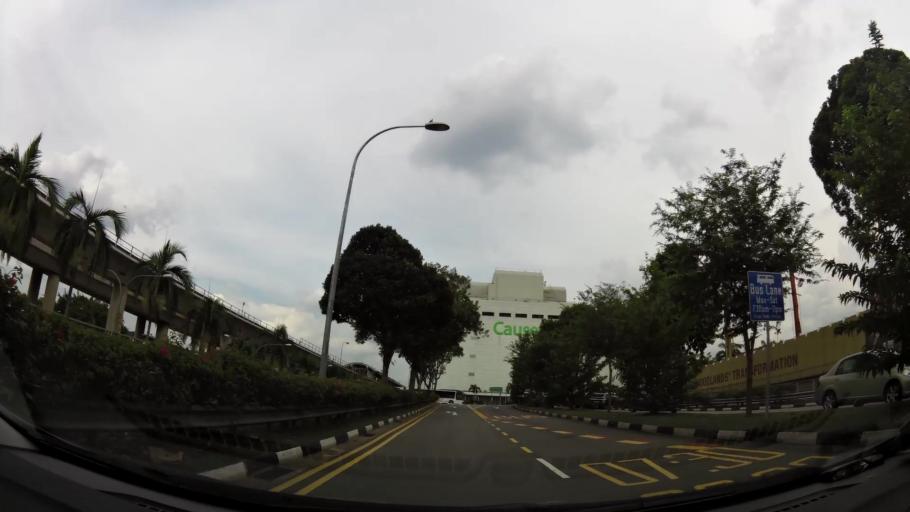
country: MY
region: Johor
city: Johor Bahru
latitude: 1.4357
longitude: 103.7843
